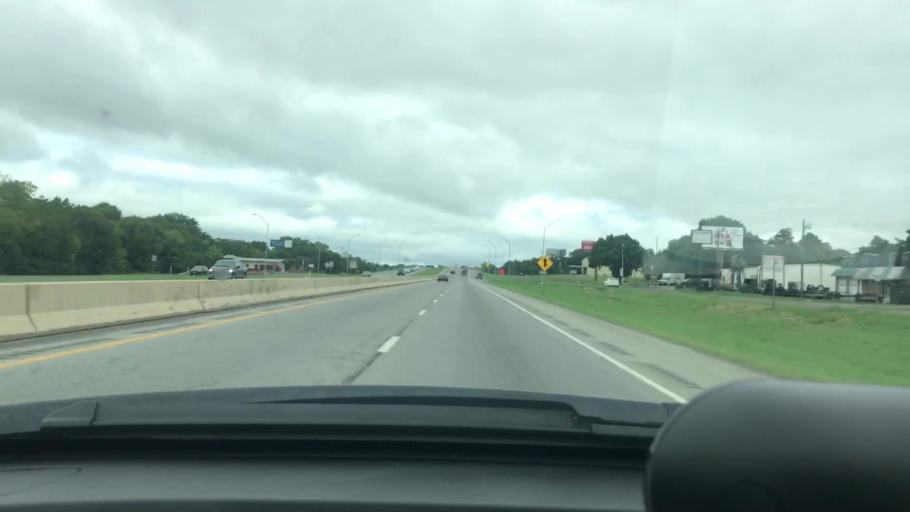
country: US
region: Texas
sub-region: Grayson County
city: Sherman
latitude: 33.6240
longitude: -96.6121
